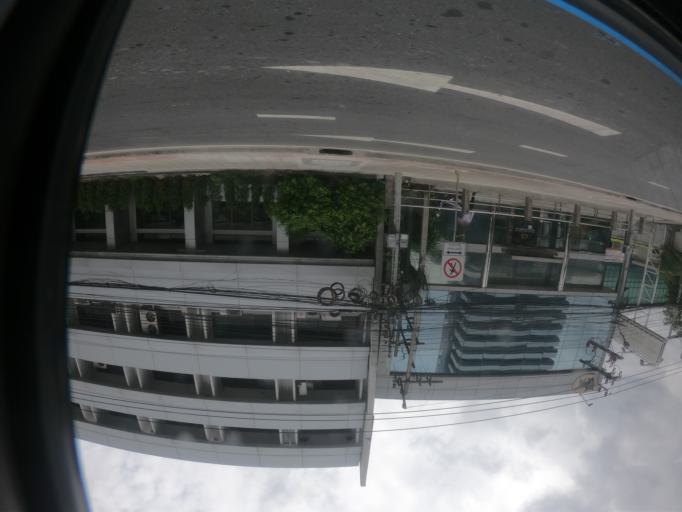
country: TH
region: Bangkok
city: Suan Luang
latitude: 13.7386
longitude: 100.6263
